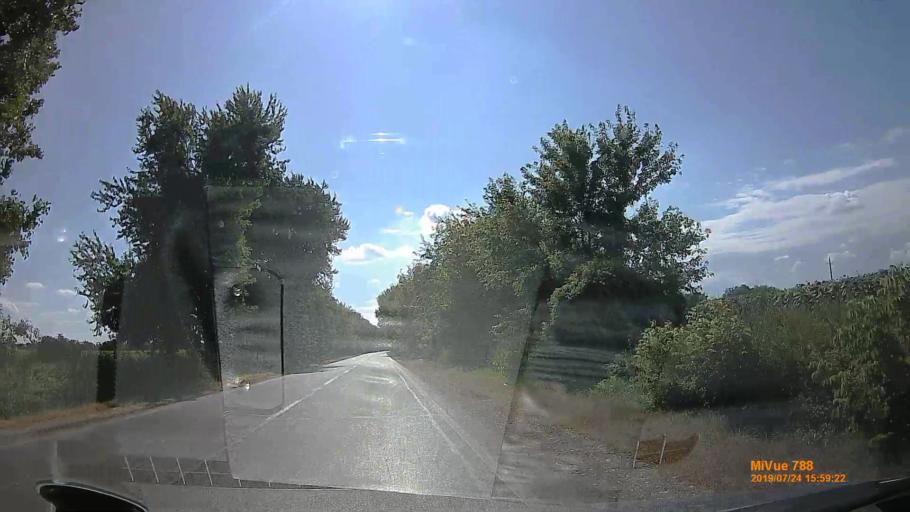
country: HU
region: Szabolcs-Szatmar-Bereg
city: Ofeherto
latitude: 47.9783
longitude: 22.0396
